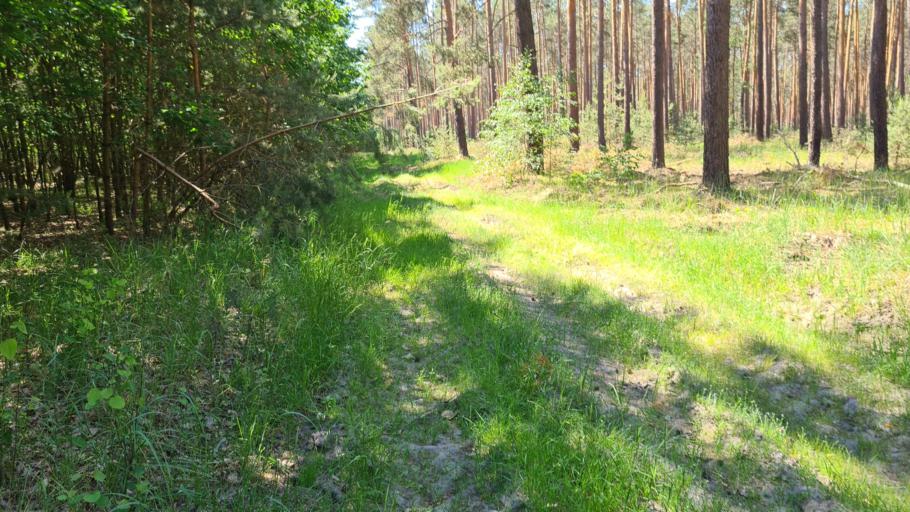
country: DE
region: Brandenburg
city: Schlieben
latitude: 51.7782
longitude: 13.3583
